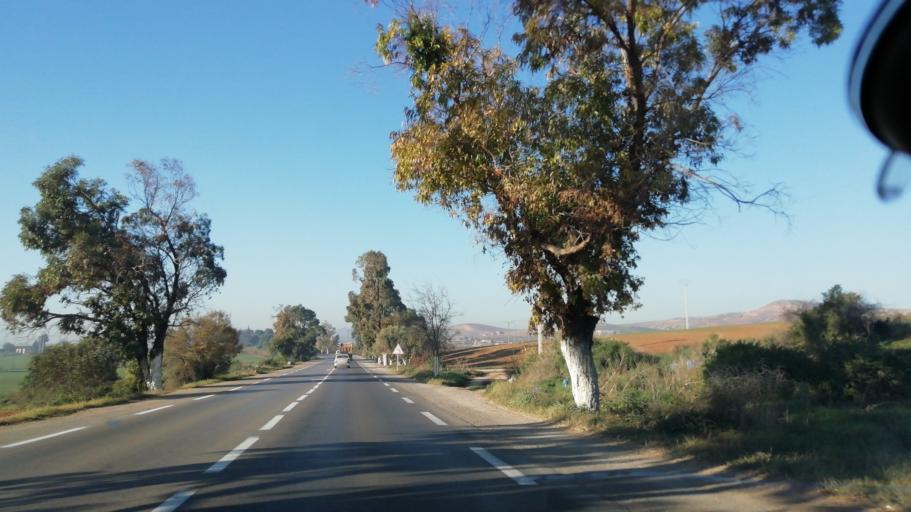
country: DZ
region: Tlemcen
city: Remchi
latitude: 35.0624
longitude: -1.4874
